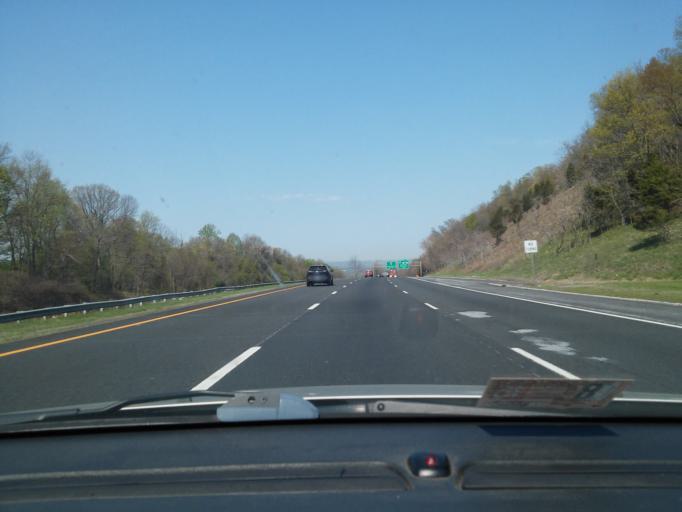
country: US
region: New Jersey
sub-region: Somerset County
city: Green Knoll
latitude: 40.6429
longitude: -74.6164
